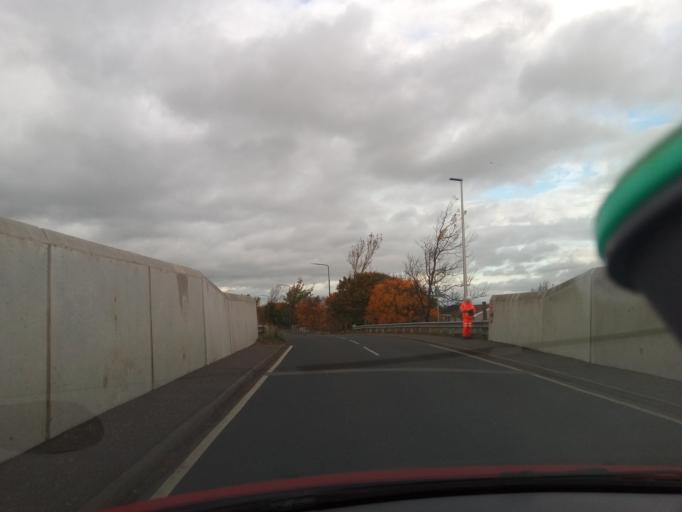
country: GB
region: Scotland
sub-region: West Lothian
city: Blackburn
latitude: 55.8412
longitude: -3.6145
